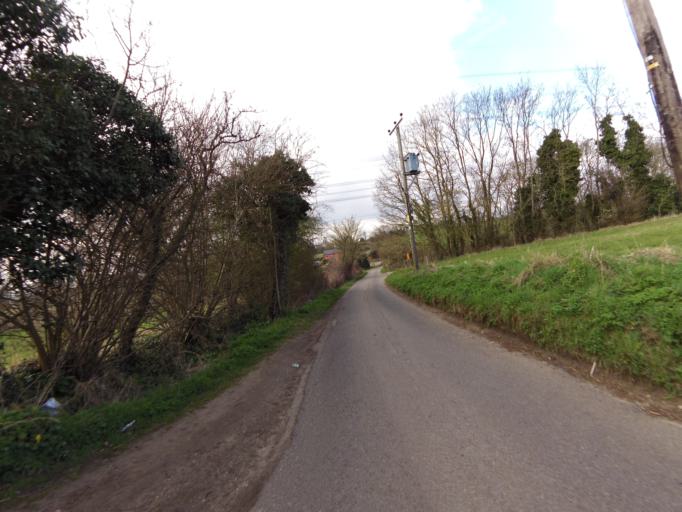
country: GB
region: England
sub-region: Suffolk
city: Ipswich
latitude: 52.0904
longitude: 1.1337
